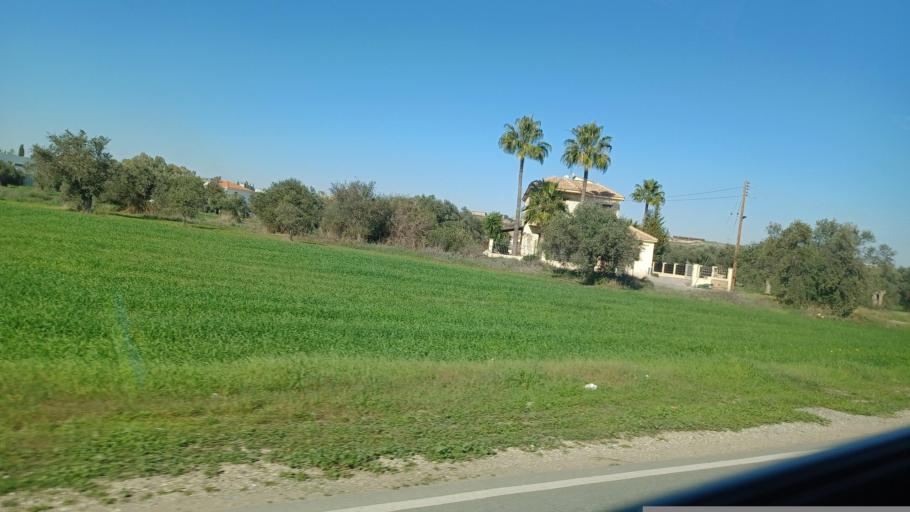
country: CY
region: Lefkosia
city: Dali
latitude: 35.0221
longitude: 33.3989
